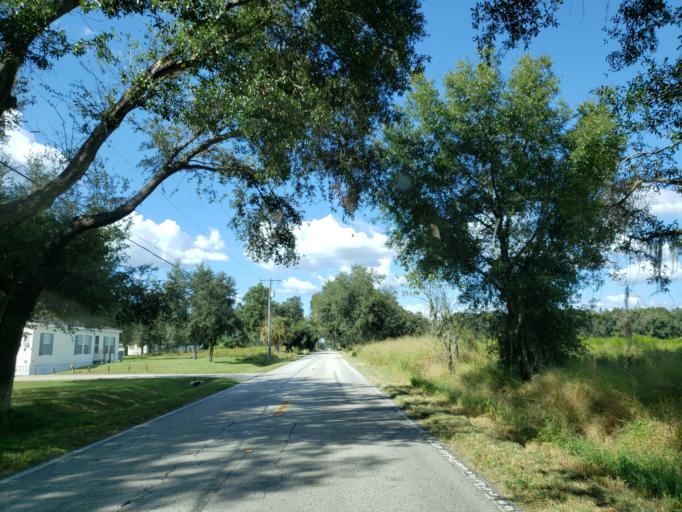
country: US
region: Florida
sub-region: Hillsborough County
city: Valrico
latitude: 27.9570
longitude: -82.2031
